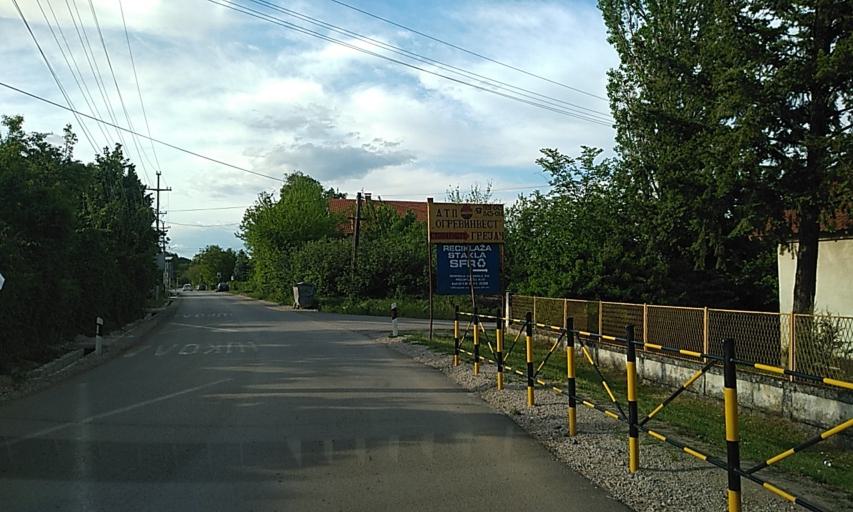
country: RS
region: Central Serbia
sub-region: Nisavski Okrug
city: Aleksinac
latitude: 43.4203
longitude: 21.7464
